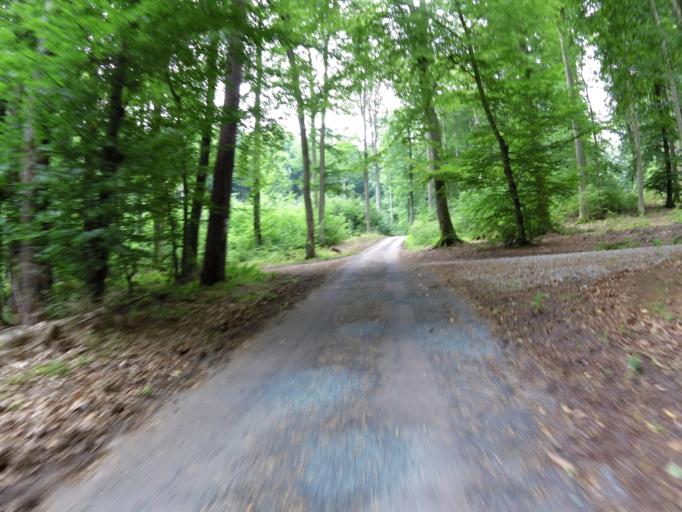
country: DE
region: Mecklenburg-Vorpommern
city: Seebad Heringsdorf
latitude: 53.9057
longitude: 14.1625
